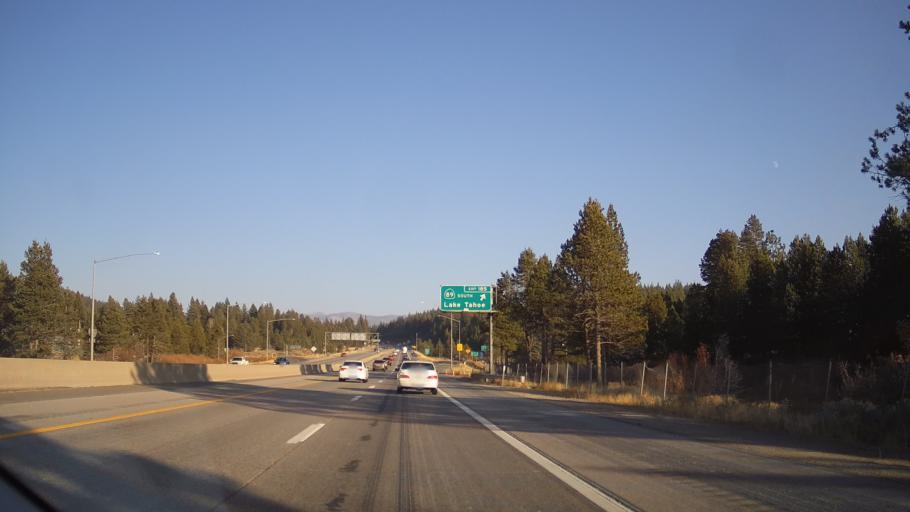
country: US
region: California
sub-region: Nevada County
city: Truckee
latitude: 39.3231
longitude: -120.2127
